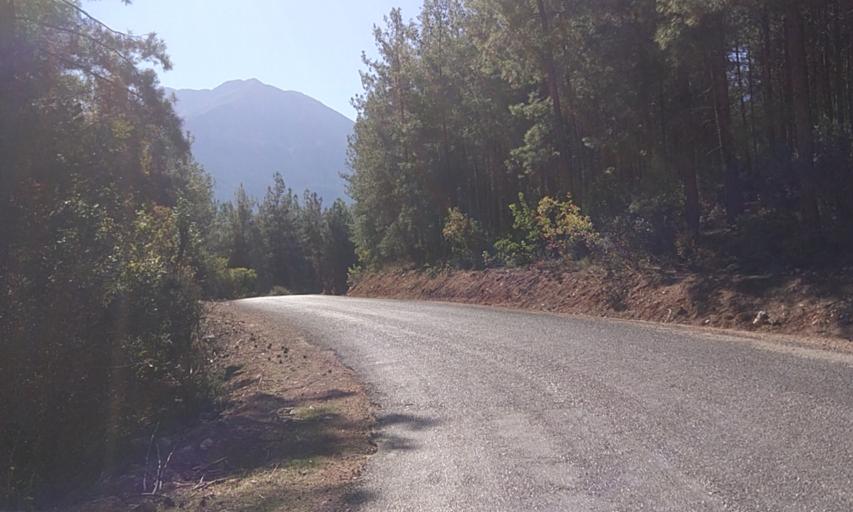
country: TR
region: Antalya
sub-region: Kemer
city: Goeynuek
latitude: 36.6262
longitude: 30.4449
